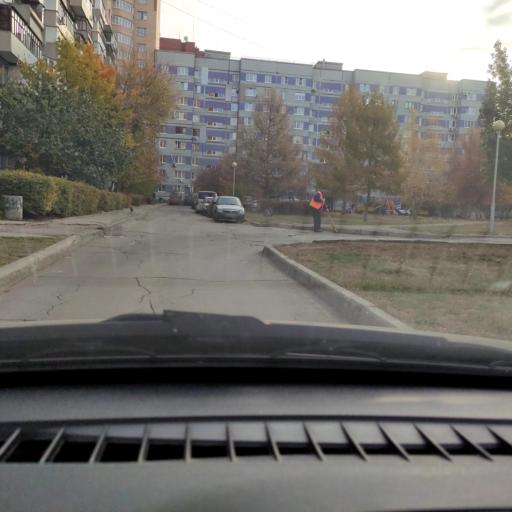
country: RU
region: Samara
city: Tol'yatti
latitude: 53.5408
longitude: 49.3398
